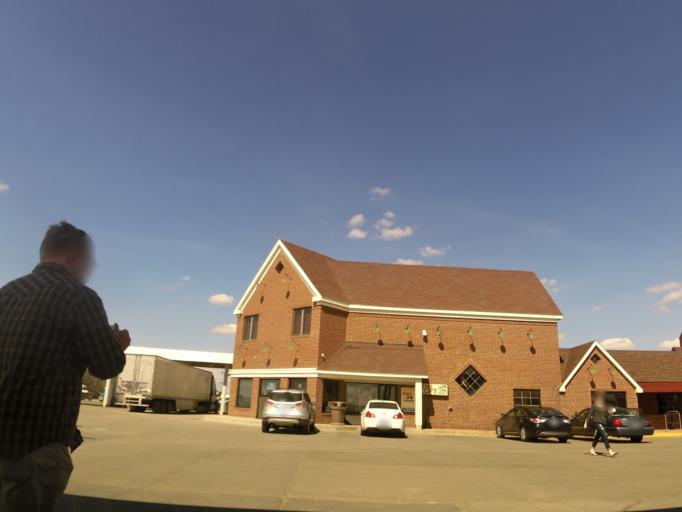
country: US
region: South Dakota
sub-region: Codington County
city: Watertown
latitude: 44.8910
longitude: -97.0541
